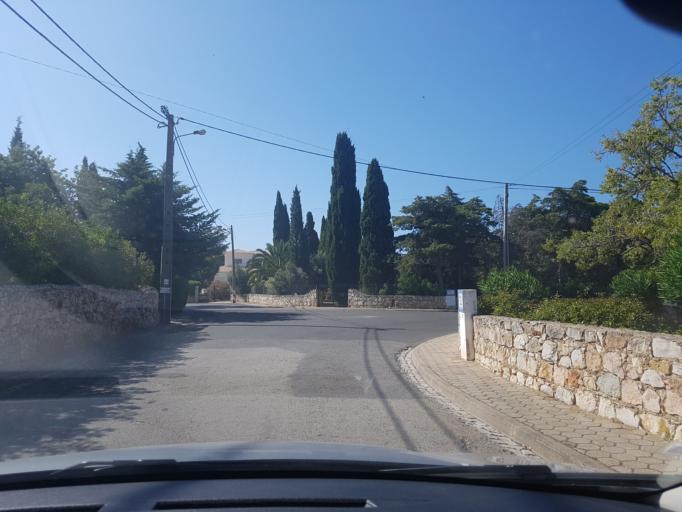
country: PT
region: Faro
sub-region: Lagoa
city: Carvoeiro
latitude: 37.0990
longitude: -8.4629
